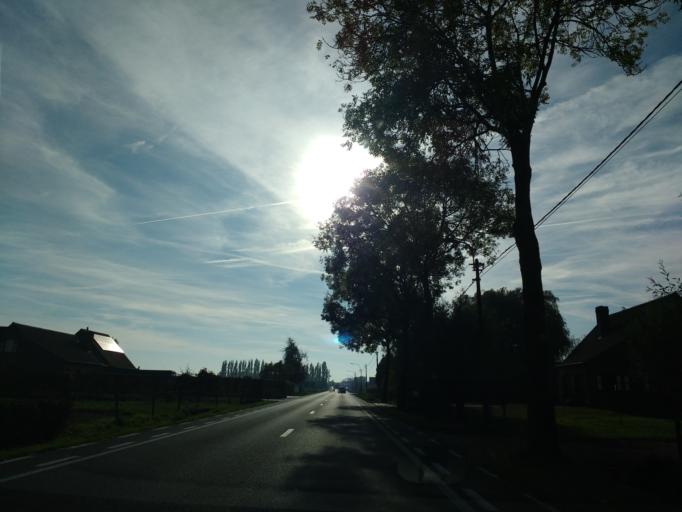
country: BE
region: Flanders
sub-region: Provincie Oost-Vlaanderen
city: Kaprijke
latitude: 51.2354
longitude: 3.6176
